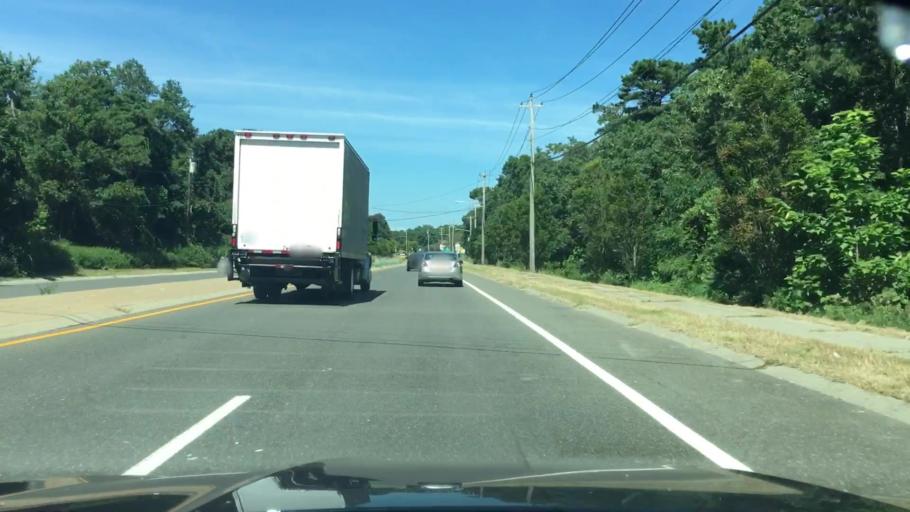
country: US
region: New York
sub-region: Suffolk County
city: Coram
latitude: 40.8863
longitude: -73.0119
